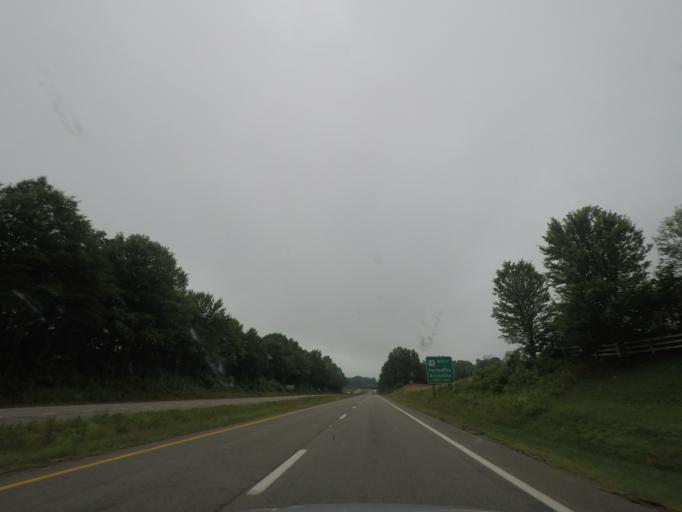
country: US
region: Virginia
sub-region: Charlotte County
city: Charlotte Court House
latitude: 37.0588
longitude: -78.4706
